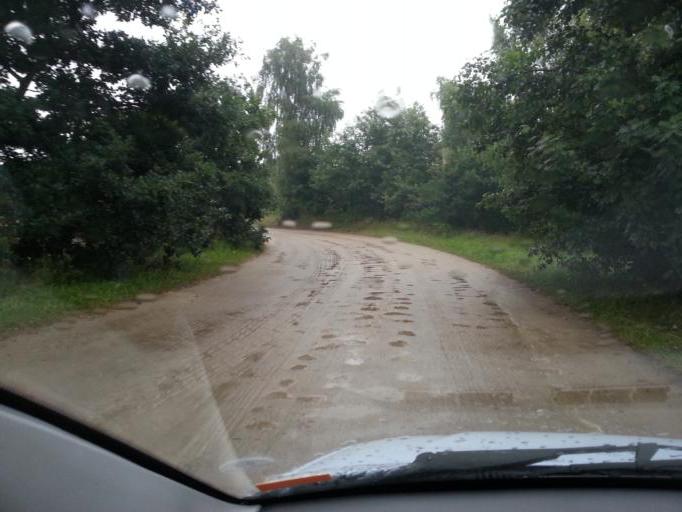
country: DK
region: South Denmark
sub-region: Vejle Kommune
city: Jelling
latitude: 55.8076
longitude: 9.3514
